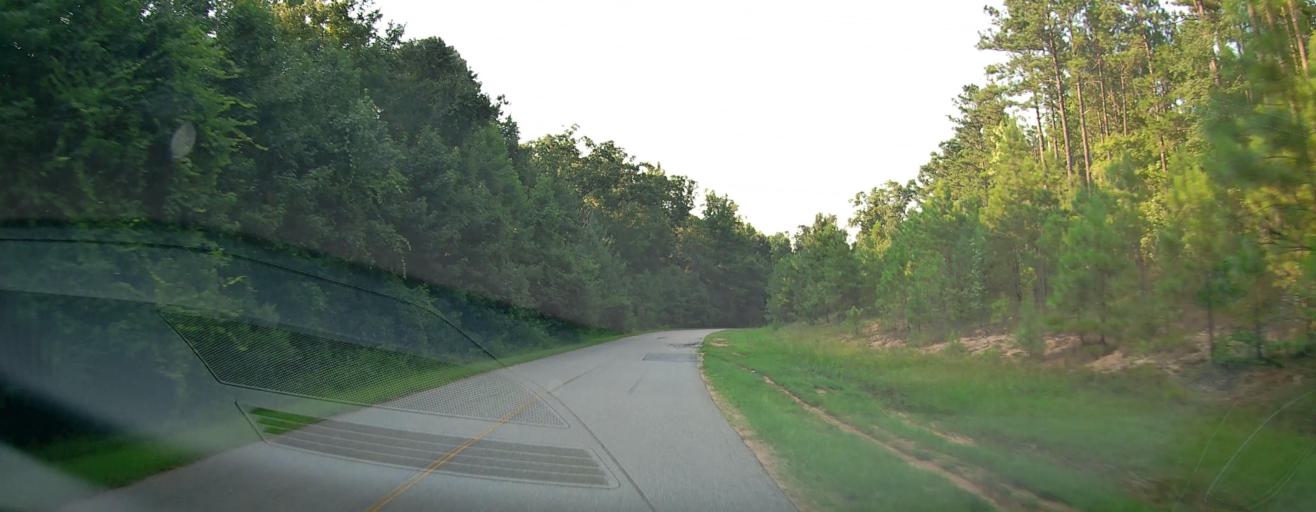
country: US
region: Georgia
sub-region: Bibb County
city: West Point
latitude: 32.8828
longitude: -83.8300
